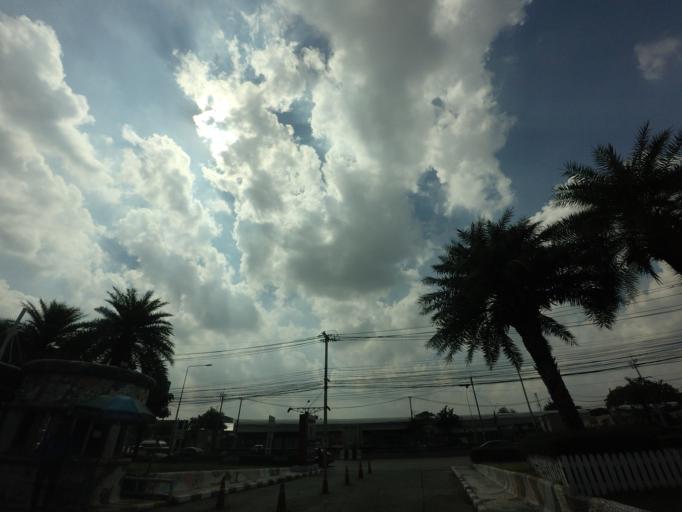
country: TH
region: Bangkok
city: Lat Phrao
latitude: 13.8206
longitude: 100.6343
